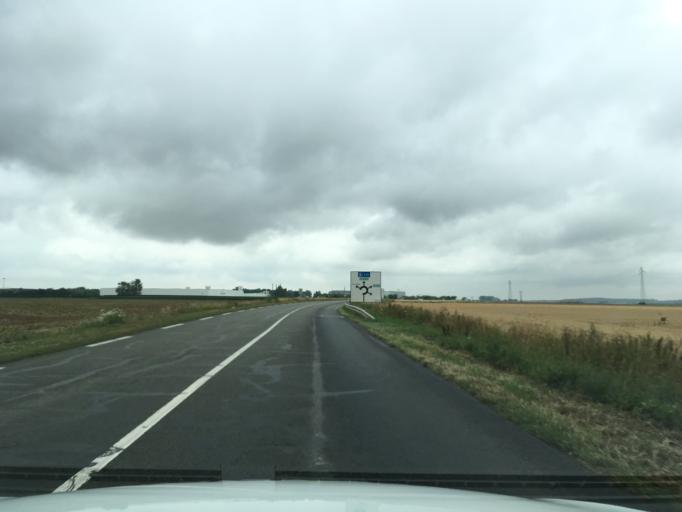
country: FR
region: Picardie
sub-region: Departement de la Somme
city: Roisel
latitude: 49.8782
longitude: 3.0576
